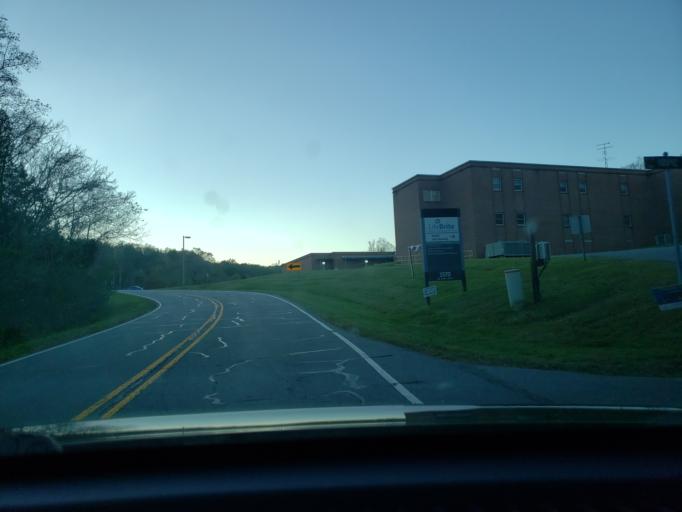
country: US
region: North Carolina
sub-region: Stokes County
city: Danbury
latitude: 36.4175
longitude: -80.2298
